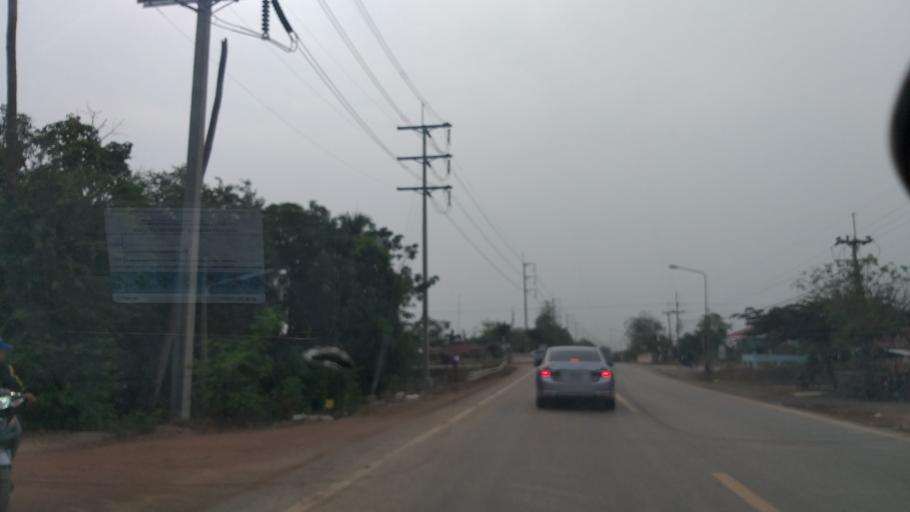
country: TH
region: Chachoengsao
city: Plaeng Yao
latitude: 13.5844
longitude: 101.2208
